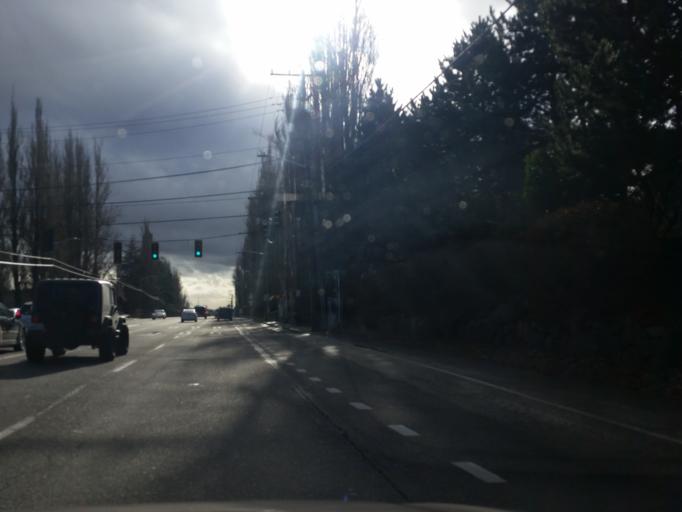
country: US
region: Washington
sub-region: King County
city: Shoreline
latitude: 47.7128
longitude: -122.3449
